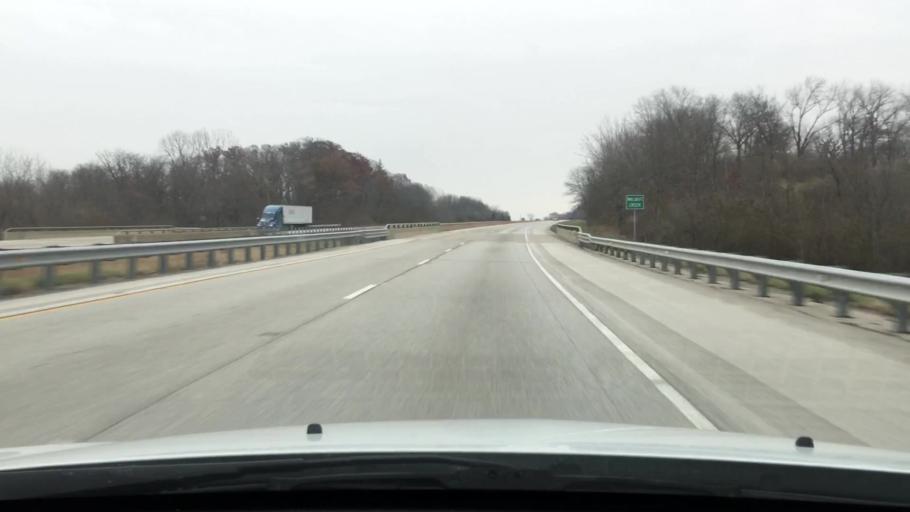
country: US
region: Illinois
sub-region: Scott County
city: Winchester
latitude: 39.6812
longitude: -90.3956
